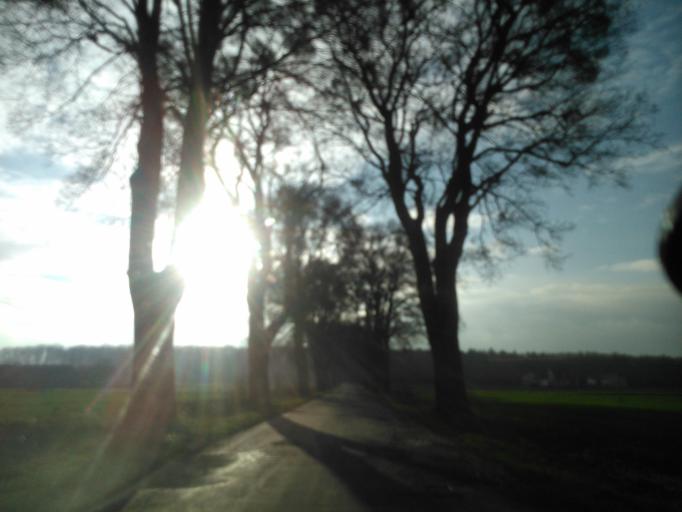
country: PL
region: Kujawsko-Pomorskie
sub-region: Powiat wabrzeski
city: Debowa Laka
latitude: 53.2069
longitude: 19.1157
